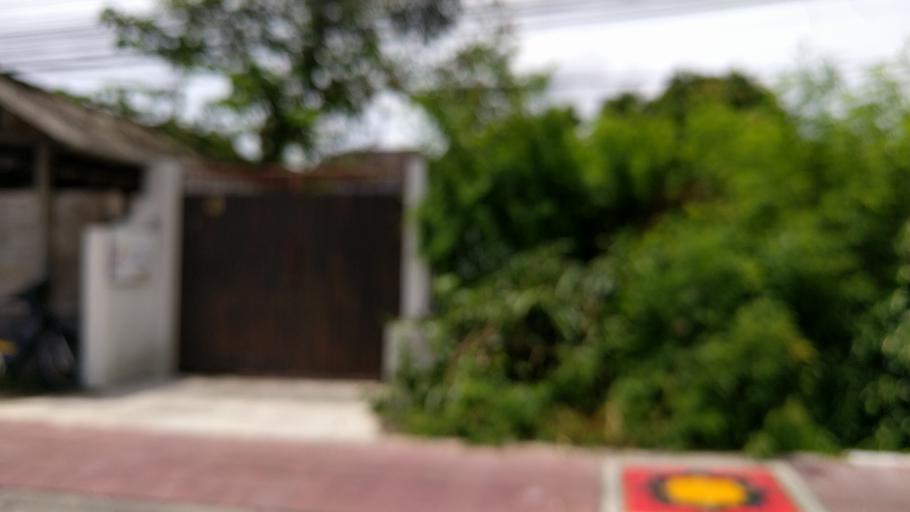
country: ID
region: Bali
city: Kuta
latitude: -8.6716
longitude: 115.1594
